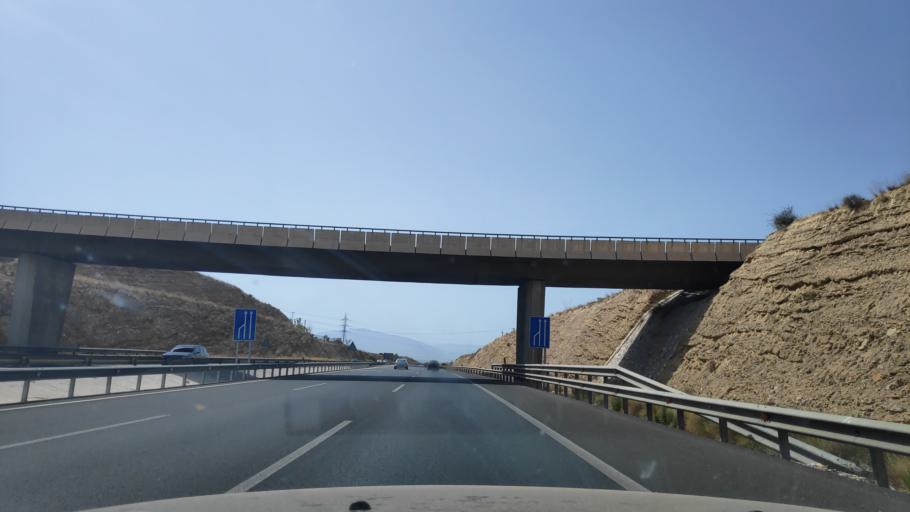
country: ES
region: Murcia
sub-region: Murcia
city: Molina de Segura
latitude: 38.0461
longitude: -1.1675
